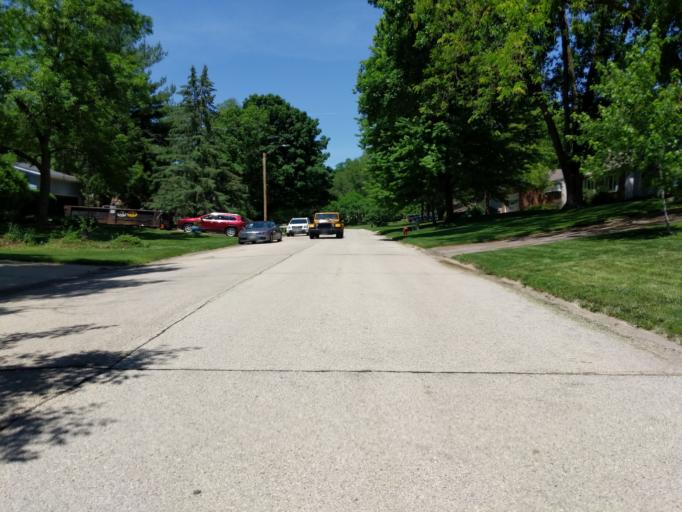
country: US
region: Iowa
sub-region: Linn County
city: Cedar Rapids
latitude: 42.0176
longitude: -91.6244
